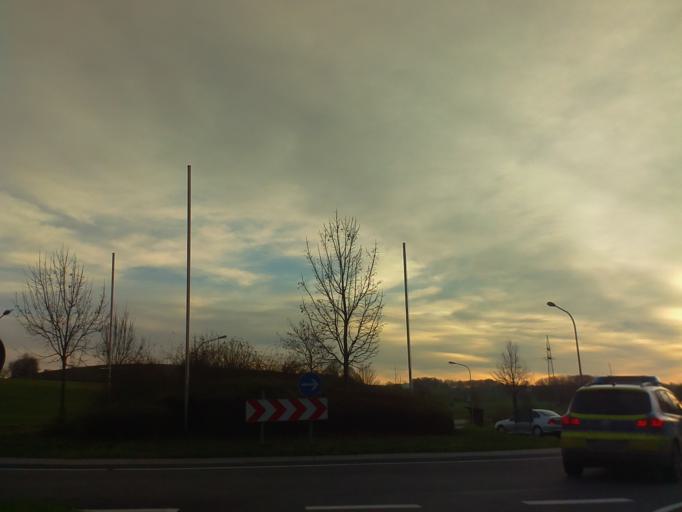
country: DE
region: Hesse
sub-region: Regierungsbezirk Darmstadt
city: Rimbach
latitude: 49.6099
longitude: 8.7541
